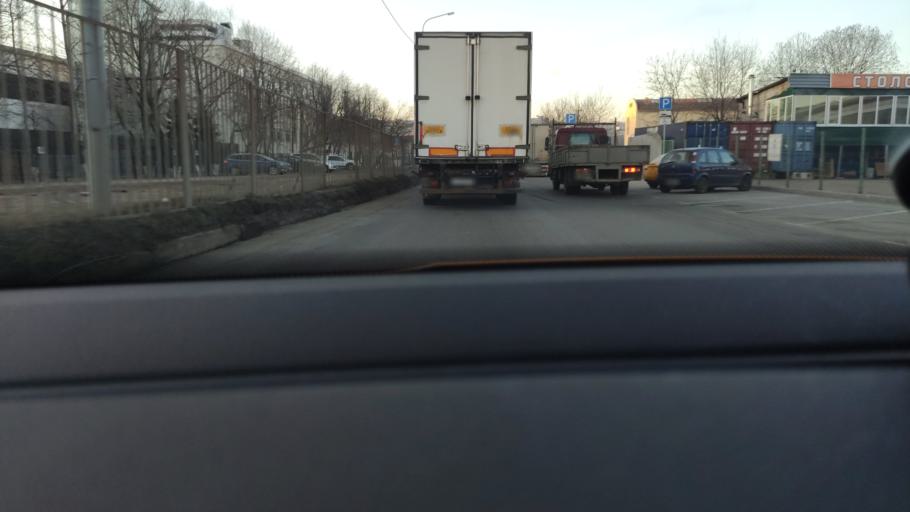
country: RU
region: Moskovskaya
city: Vostochnoe Degunino
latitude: 55.8862
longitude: 37.5528
